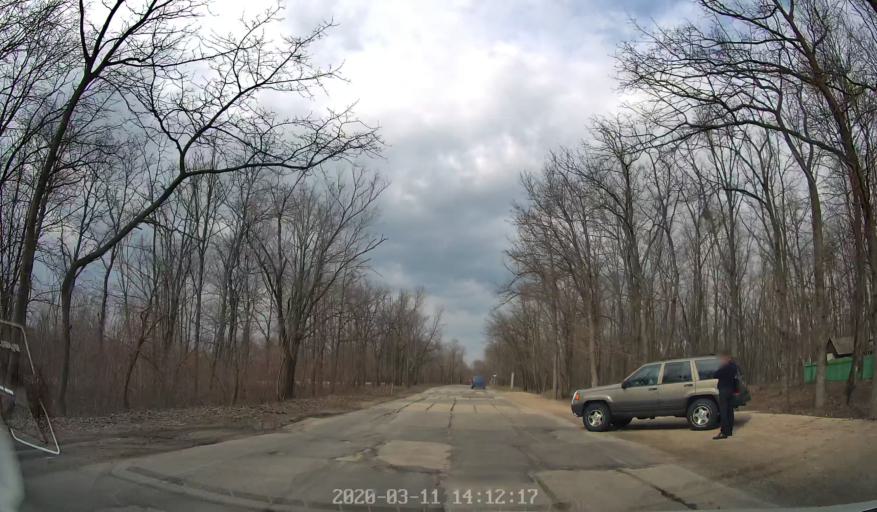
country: MD
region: Chisinau
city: Stauceni
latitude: 47.0520
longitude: 28.8837
